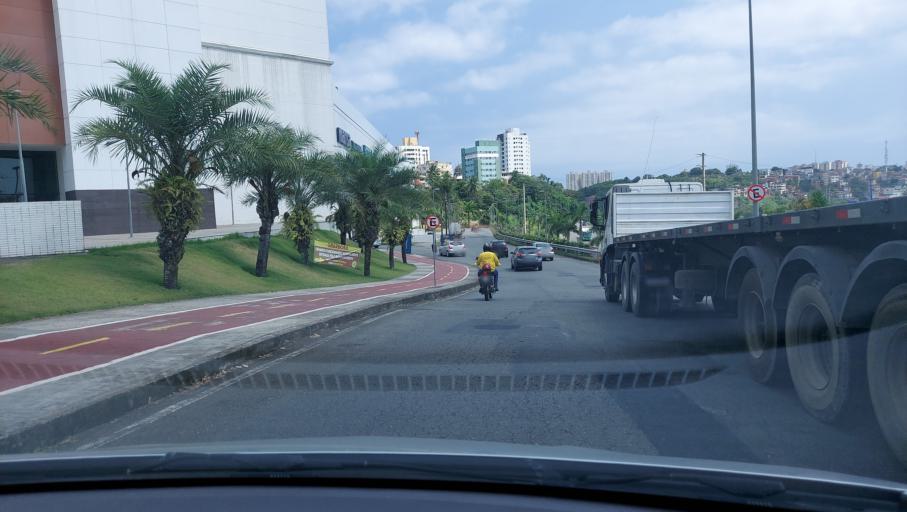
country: BR
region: Bahia
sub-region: Salvador
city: Salvador
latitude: -12.9699
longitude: -38.4752
